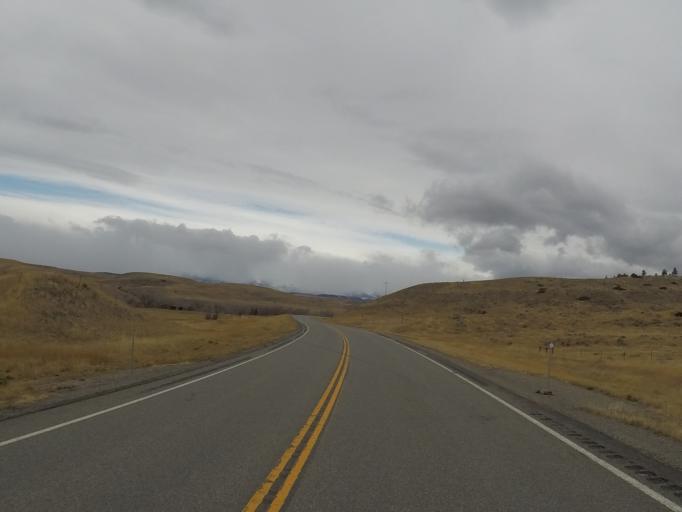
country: US
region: Montana
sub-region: Sweet Grass County
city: Big Timber
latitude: 45.8994
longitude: -109.9677
